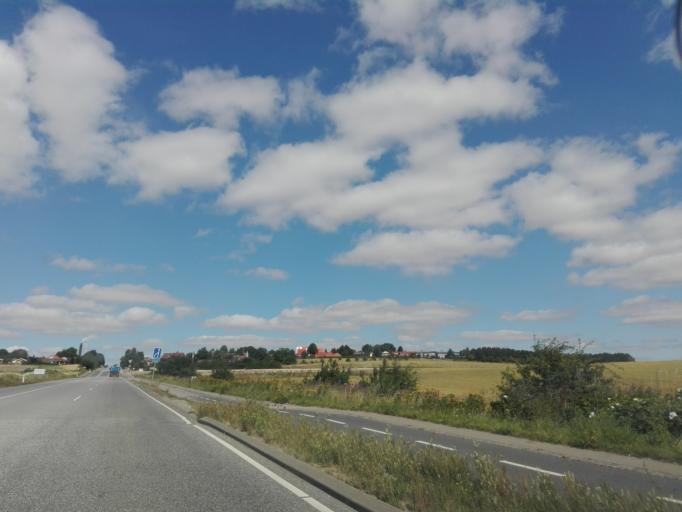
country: DK
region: Central Jutland
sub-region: Arhus Kommune
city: Trige
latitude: 56.2152
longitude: 10.1697
